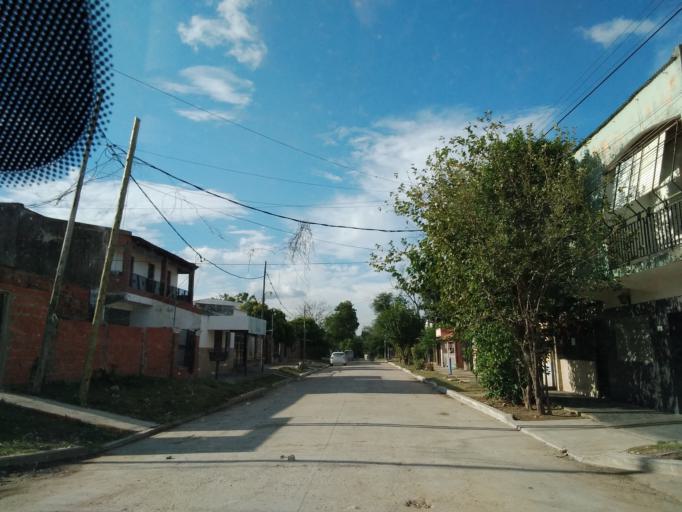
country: AR
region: Corrientes
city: Corrientes
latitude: -27.4604
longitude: -58.8164
